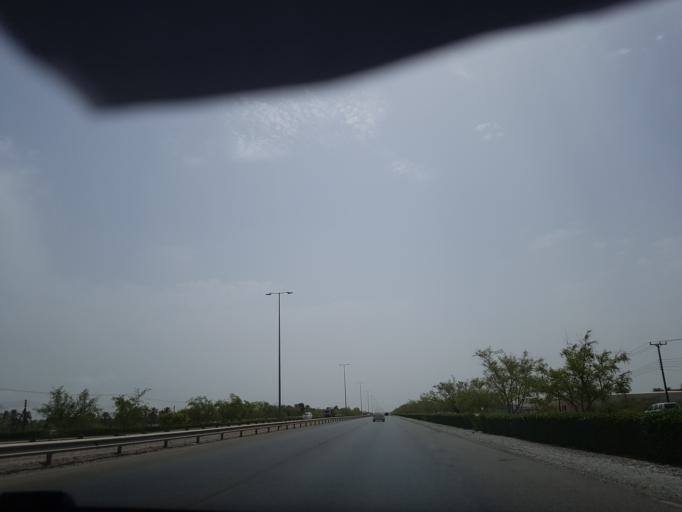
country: OM
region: Al Batinah
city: Barka'
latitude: 23.7329
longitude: 57.6899
